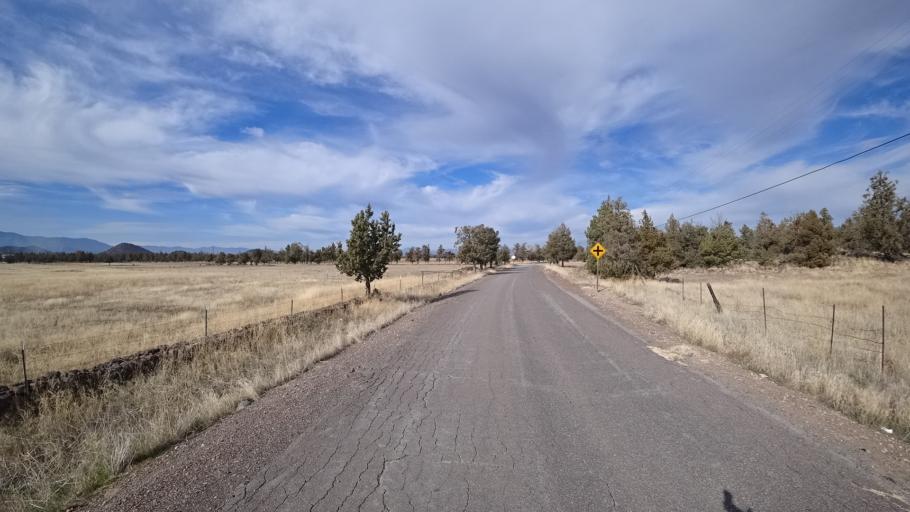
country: US
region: California
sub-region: Siskiyou County
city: Weed
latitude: 41.5942
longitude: -122.4028
